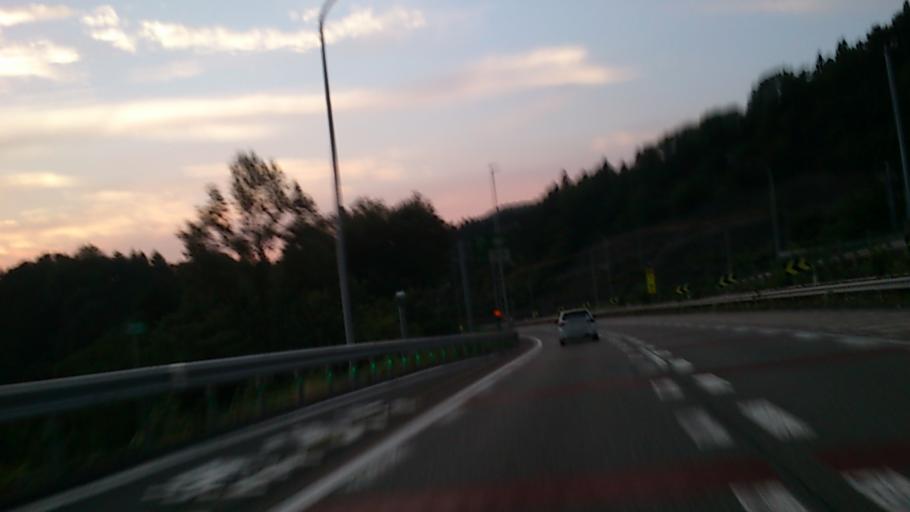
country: JP
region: Gifu
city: Nakatsugawa
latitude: 35.5068
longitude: 137.5890
